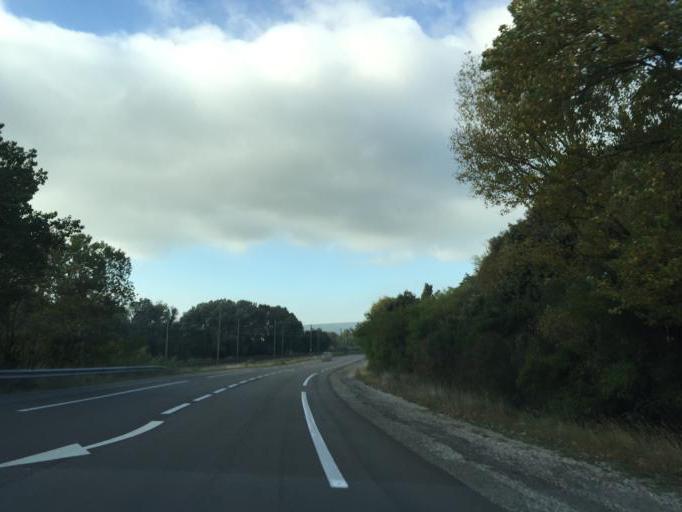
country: FR
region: Rhone-Alpes
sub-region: Departement de la Drome
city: Donzere
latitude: 44.4409
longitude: 4.6789
